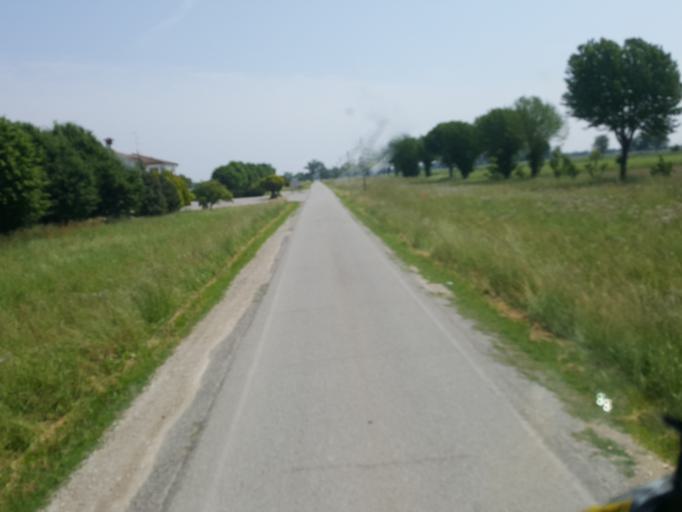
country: IT
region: Lombardy
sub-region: Provincia di Lodi
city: Boffalora d'Adda
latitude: 45.3636
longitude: 9.5113
